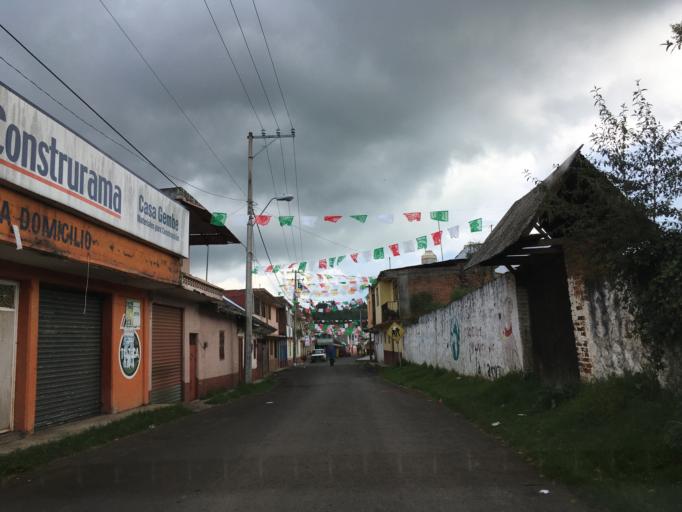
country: MX
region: Michoacan
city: Capula
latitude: 19.6446
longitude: -101.8287
